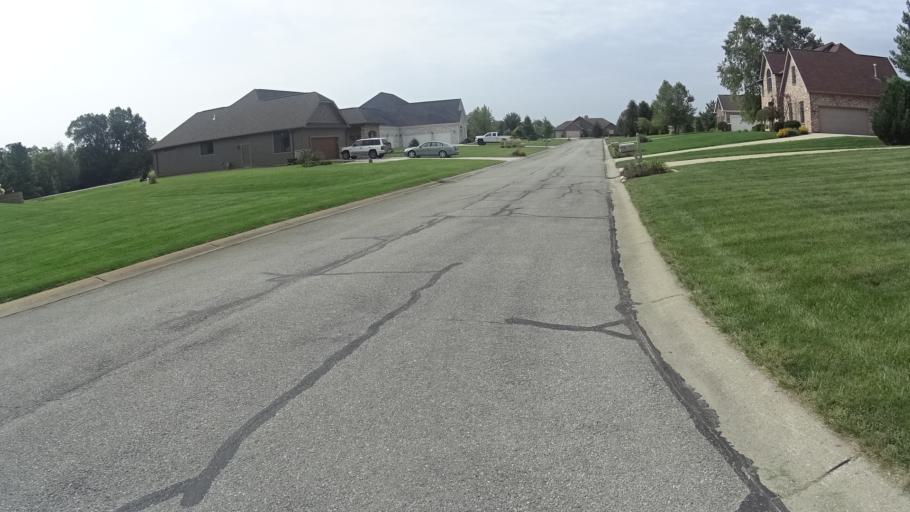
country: US
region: Indiana
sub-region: Madison County
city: Pendleton
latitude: 40.0130
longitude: -85.7924
